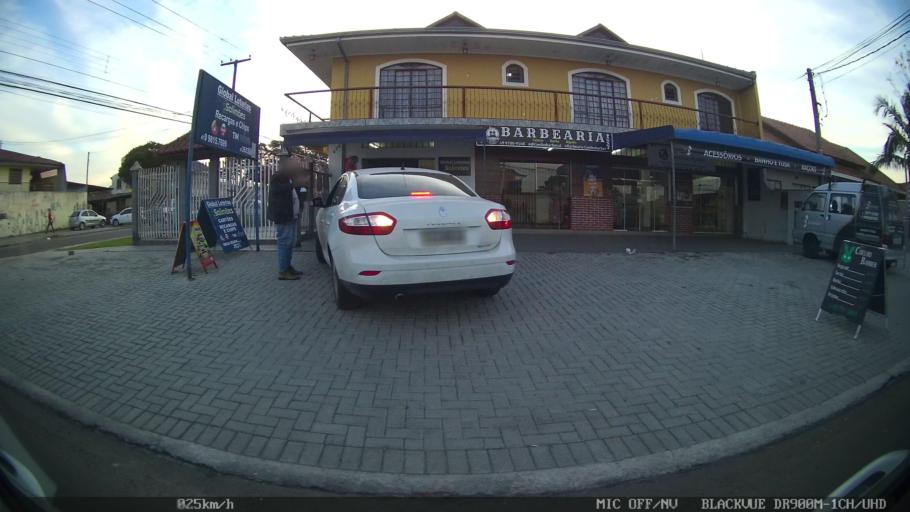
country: BR
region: Parana
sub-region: Pinhais
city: Pinhais
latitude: -25.4546
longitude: -49.1826
